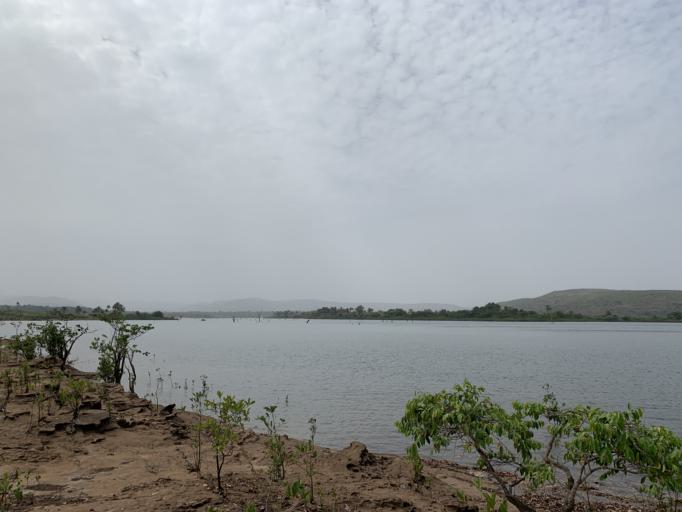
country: GN
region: Kindia
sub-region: Kindia
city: Kindia
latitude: 9.9682
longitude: -12.9861
